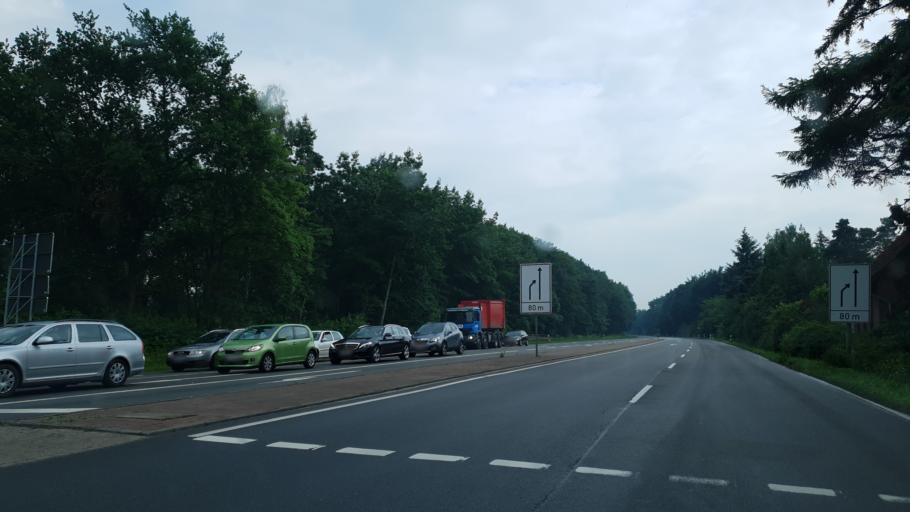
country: DE
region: Lower Saxony
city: Meppen
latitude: 52.6744
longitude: 7.3023
